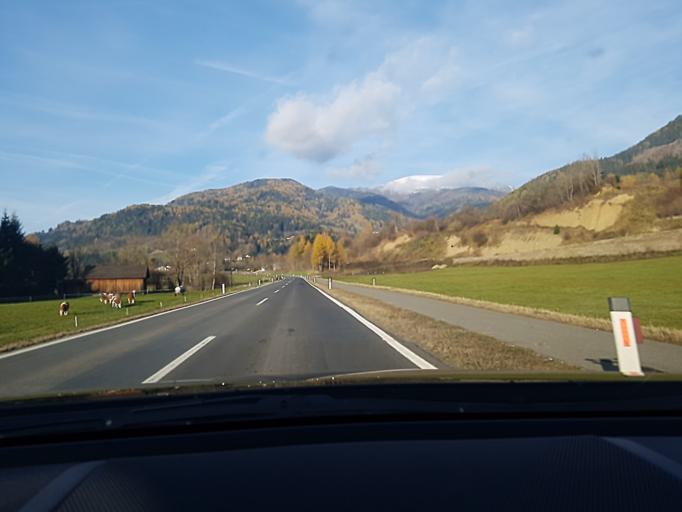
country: AT
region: Styria
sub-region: Politischer Bezirk Murau
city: Sankt Peter am Kammersberg
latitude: 47.1895
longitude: 14.1438
